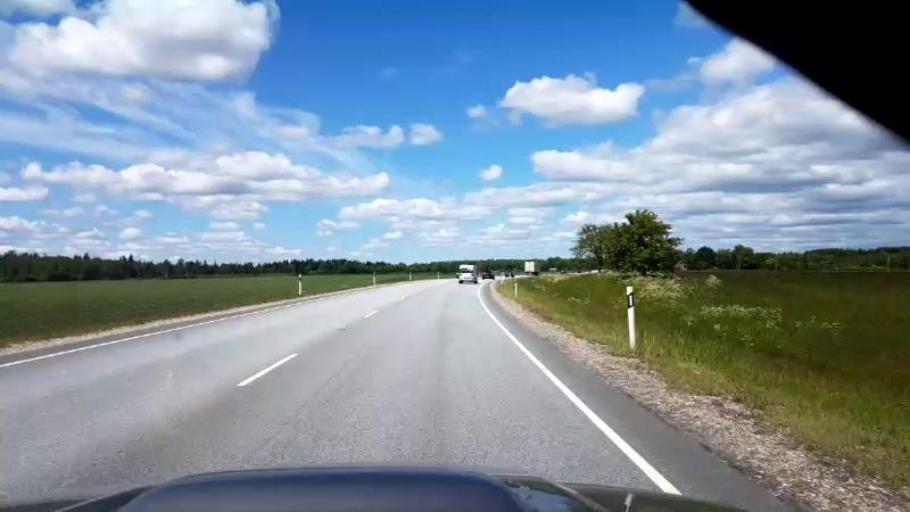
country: EE
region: Paernumaa
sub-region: Halinga vald
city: Parnu-Jaagupi
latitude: 58.5670
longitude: 24.5140
